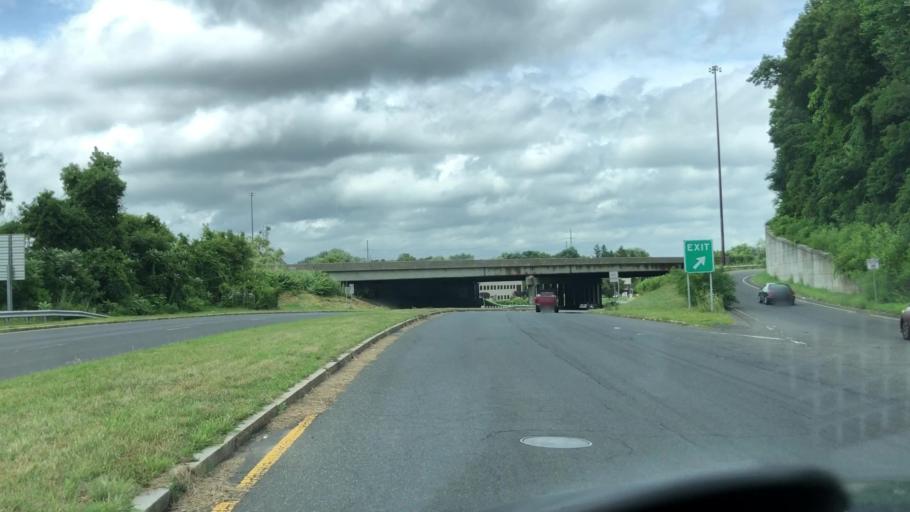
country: US
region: Massachusetts
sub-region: Hampden County
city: Chicopee
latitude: 42.1526
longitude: -72.6098
